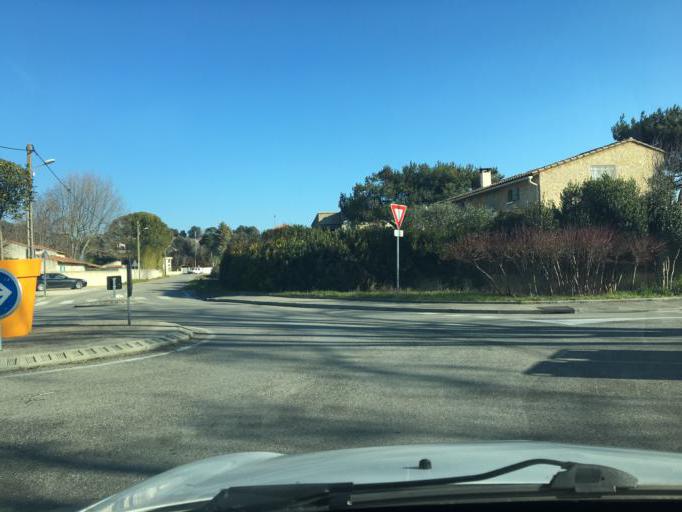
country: FR
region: Languedoc-Roussillon
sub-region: Departement du Gard
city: Les Angles
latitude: 43.9478
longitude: 4.7811
